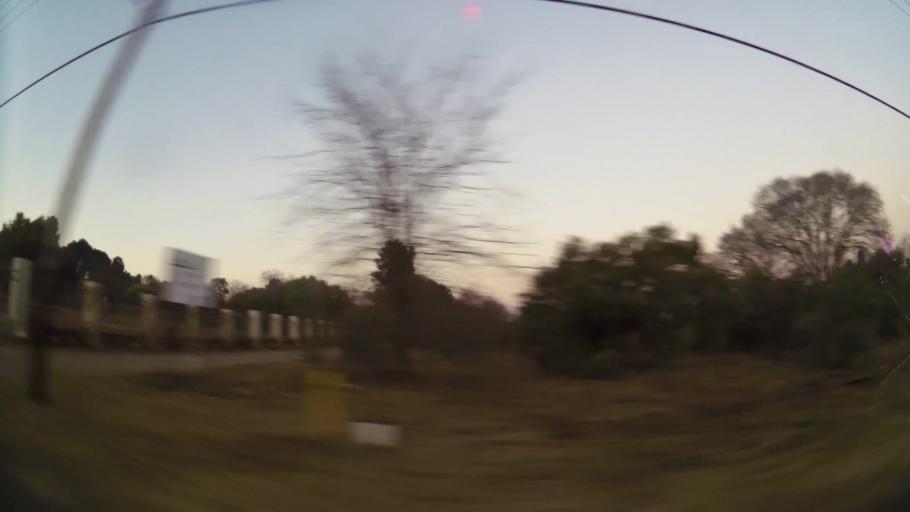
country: ZA
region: Gauteng
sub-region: City of Tshwane Metropolitan Municipality
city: Centurion
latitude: -25.8572
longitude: 28.1237
